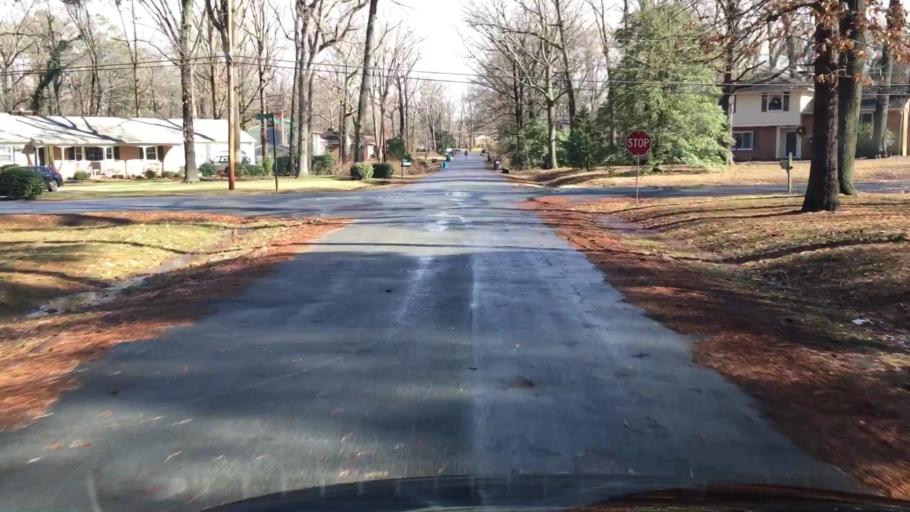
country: US
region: Virginia
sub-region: Chesterfield County
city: Bon Air
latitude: 37.5318
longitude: -77.5859
